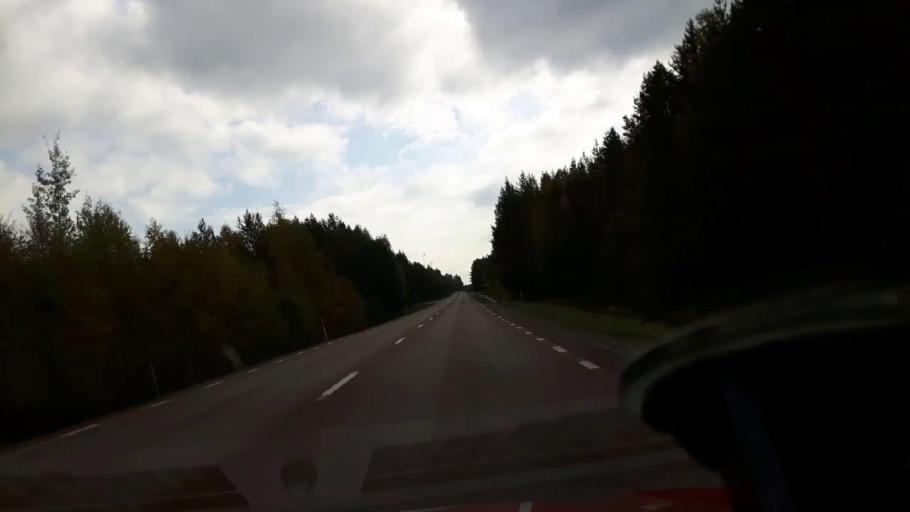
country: SE
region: Gaevleborg
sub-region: Bollnas Kommun
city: Kilafors
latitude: 61.2689
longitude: 16.5421
